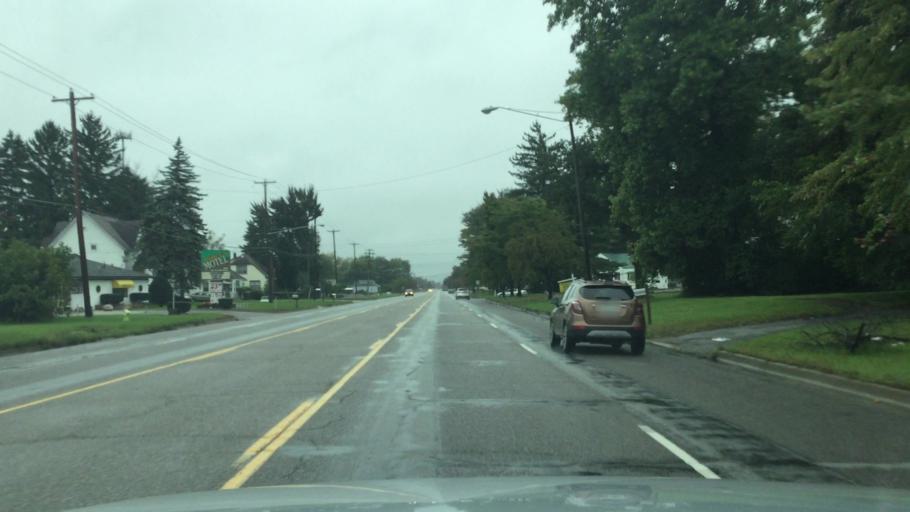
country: US
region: Michigan
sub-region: Saginaw County
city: Buena Vista
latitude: 43.3880
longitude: -83.9033
